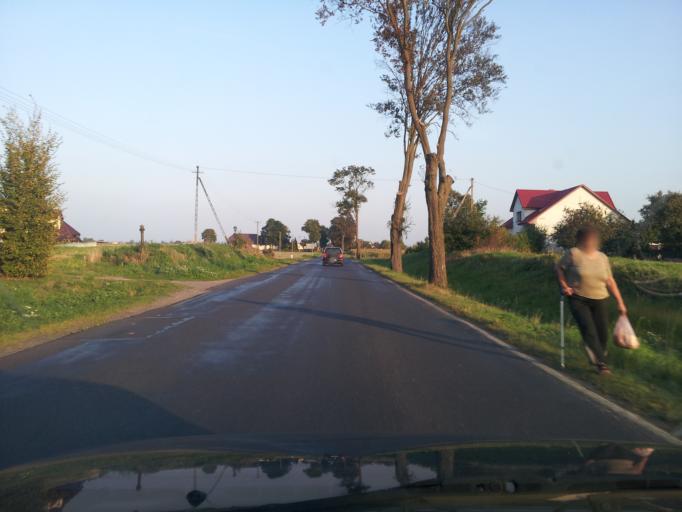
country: PL
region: Kujawsko-Pomorskie
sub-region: Powiat golubsko-dobrzynski
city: Golub-Dobrzyn
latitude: 53.1328
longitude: 19.0149
